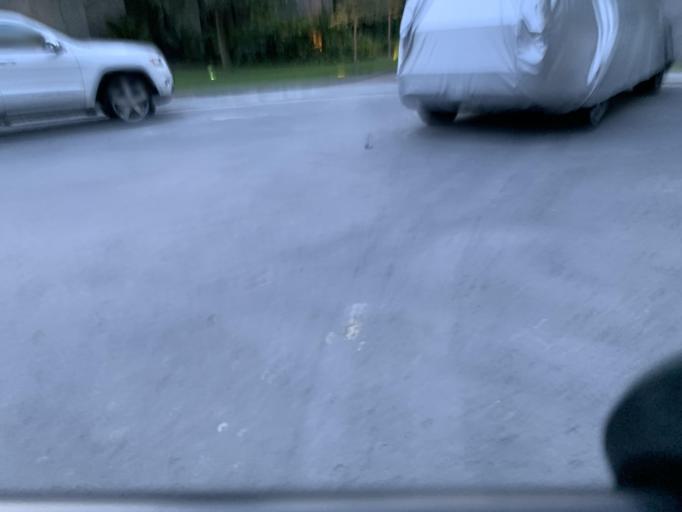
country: MX
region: Nuevo Leon
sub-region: Juarez
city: Bosques de San Pedro
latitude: 25.5222
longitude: -100.1876
